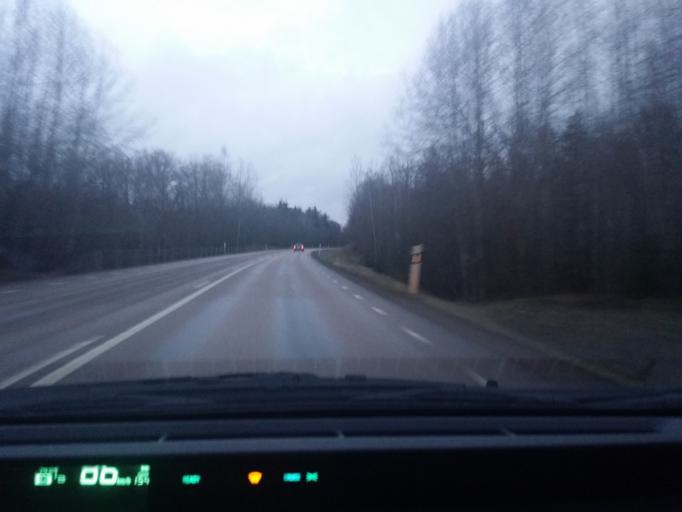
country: SE
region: Soedermanland
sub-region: Eskilstuna Kommun
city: Kvicksund
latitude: 59.4754
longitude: 16.3059
